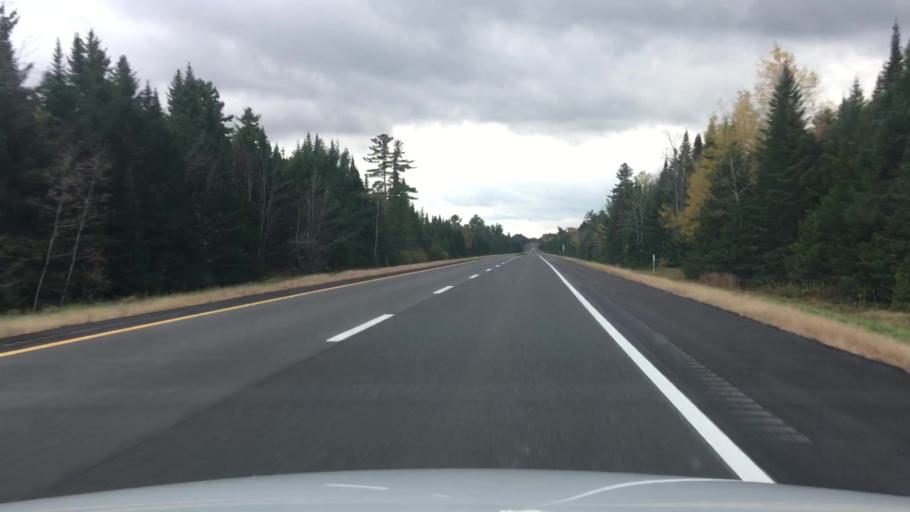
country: US
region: Maine
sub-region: Penobscot County
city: Patten
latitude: 46.0772
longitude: -68.2174
